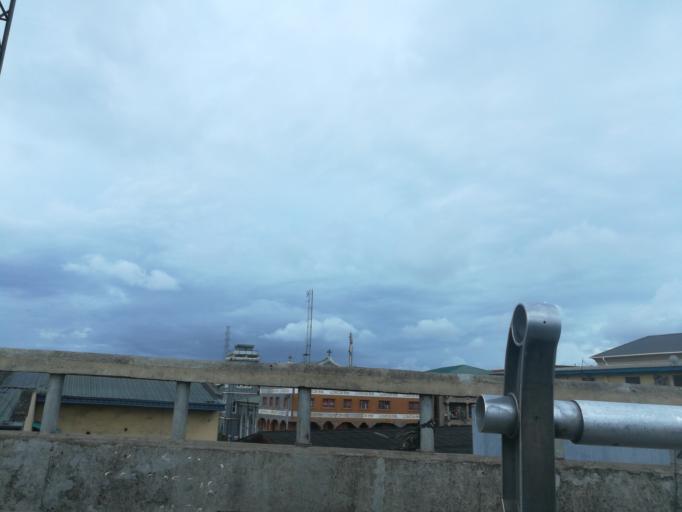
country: NG
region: Lagos
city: Lagos
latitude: 6.4641
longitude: 3.3863
